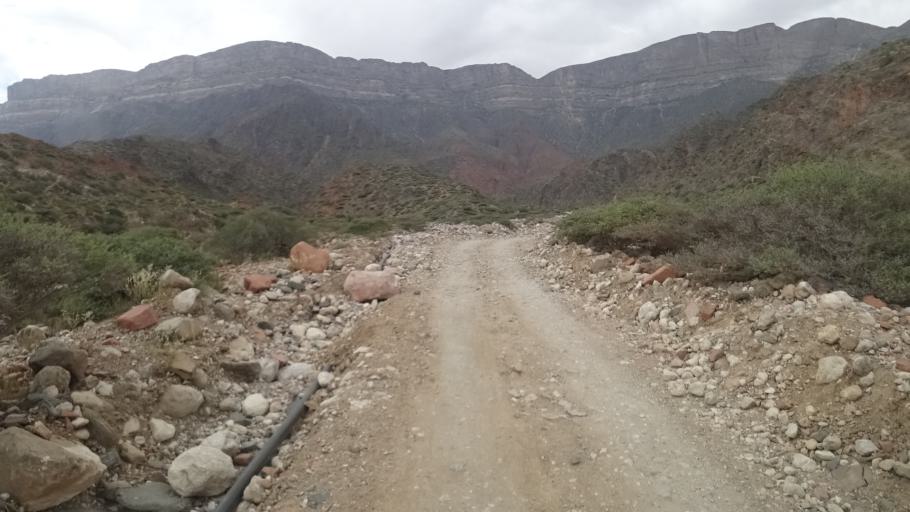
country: OM
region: Zufar
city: Salalah
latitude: 17.1783
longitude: 54.9485
